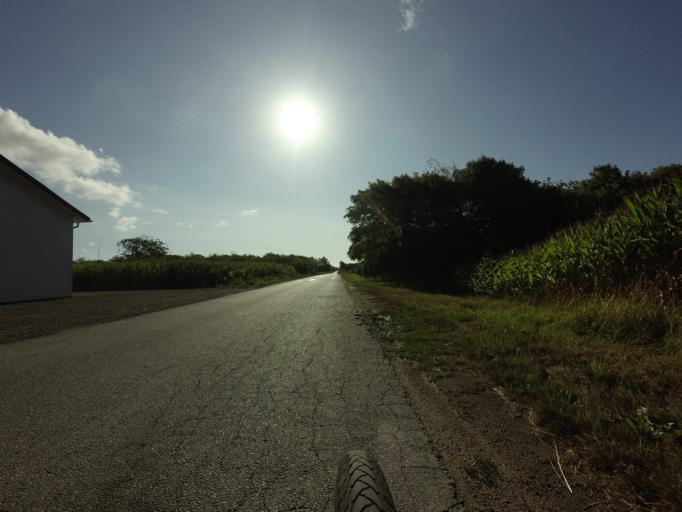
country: DK
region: North Denmark
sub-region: Hjorring Kommune
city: Vra
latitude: 57.3940
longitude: 9.9572
